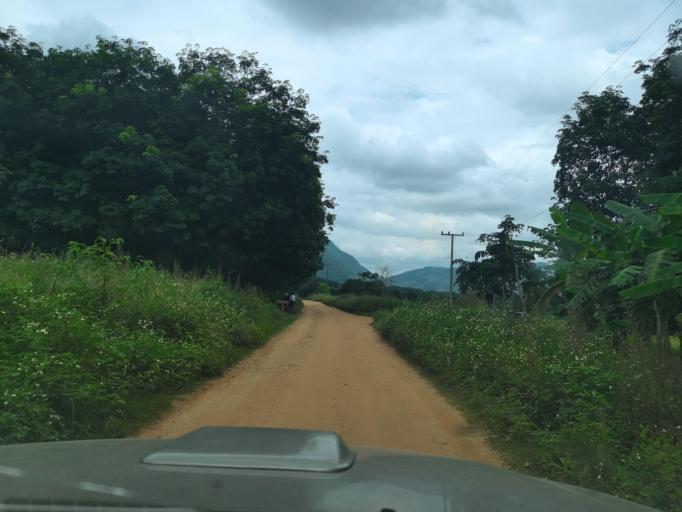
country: TH
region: Phayao
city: Phu Sang
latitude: 19.7415
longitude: 100.4484
